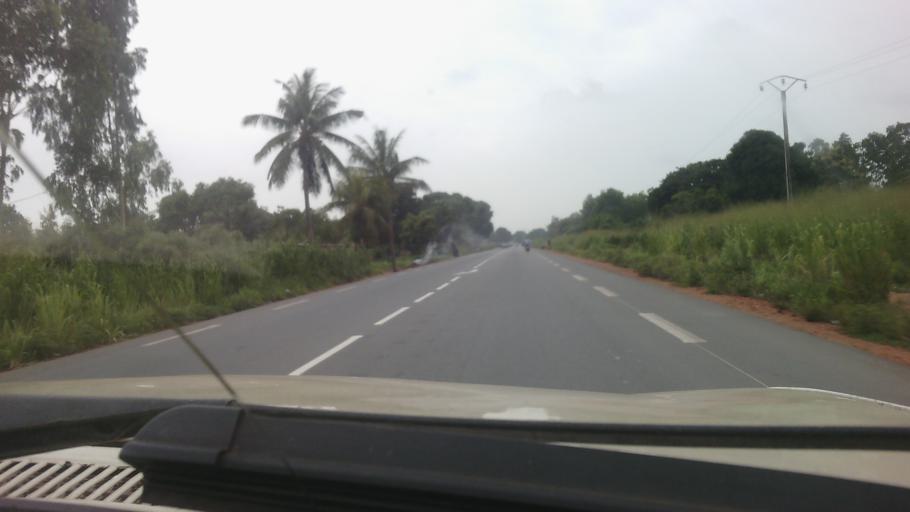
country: BJ
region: Mono
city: Come
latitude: 6.3989
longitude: 1.9576
